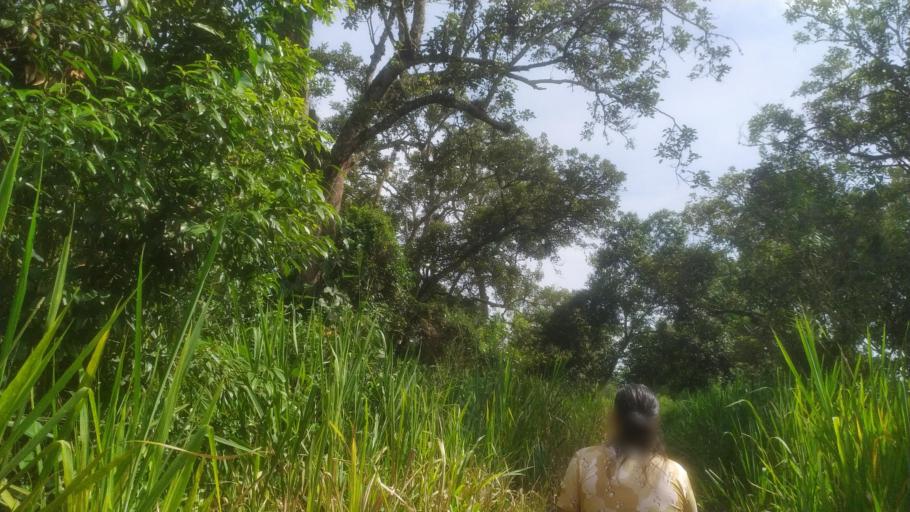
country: CO
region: Valle del Cauca
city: Jamundi
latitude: 3.2789
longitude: -76.5391
